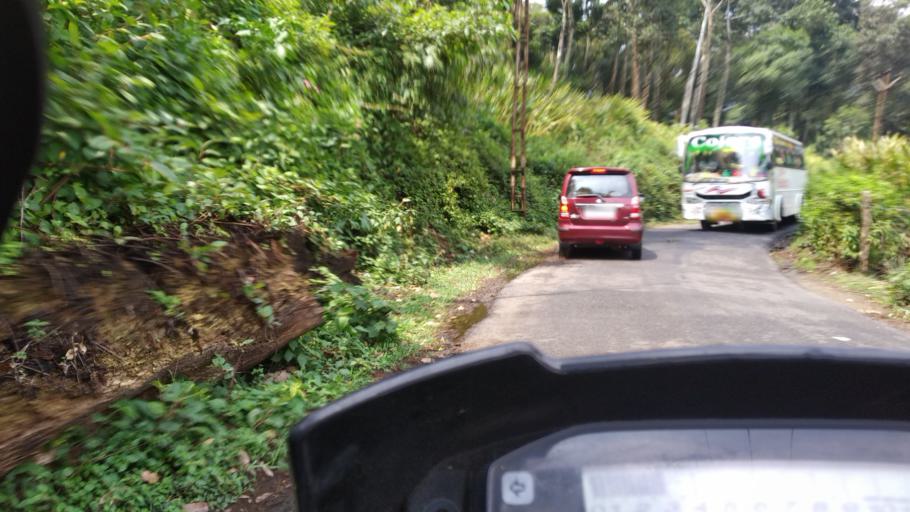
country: IN
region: Kerala
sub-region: Kottayam
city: Erattupetta
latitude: 9.6301
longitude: 76.9640
